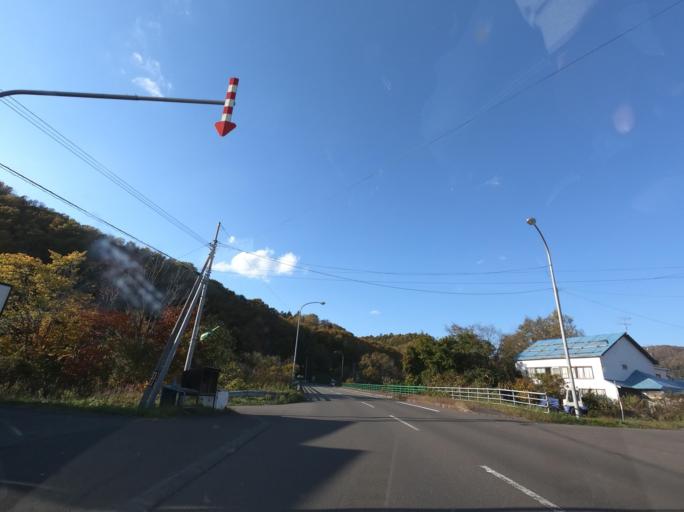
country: JP
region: Hokkaido
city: Iwamizawa
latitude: 42.9989
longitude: 142.0058
